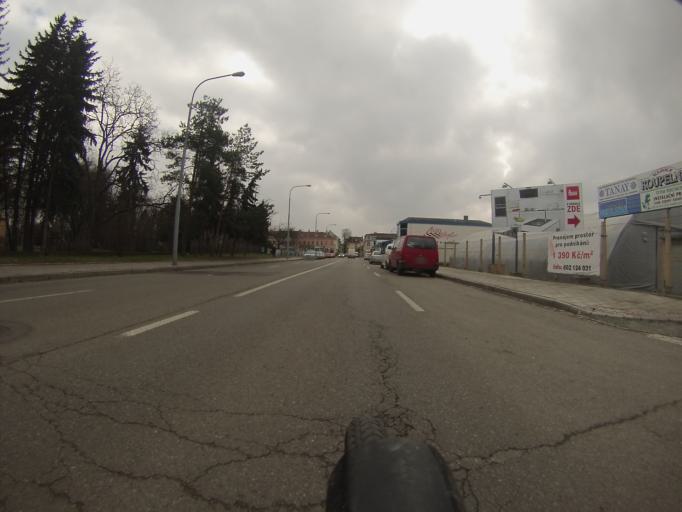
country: CZ
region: South Moravian
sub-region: Mesto Brno
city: Brno
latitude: 49.2025
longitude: 16.6381
